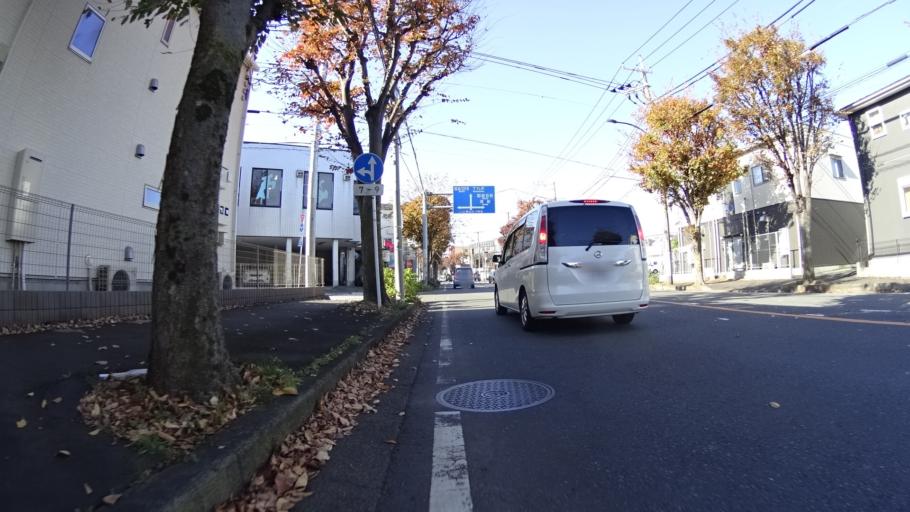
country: JP
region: Kanagawa
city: Zama
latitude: 35.5699
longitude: 139.3596
